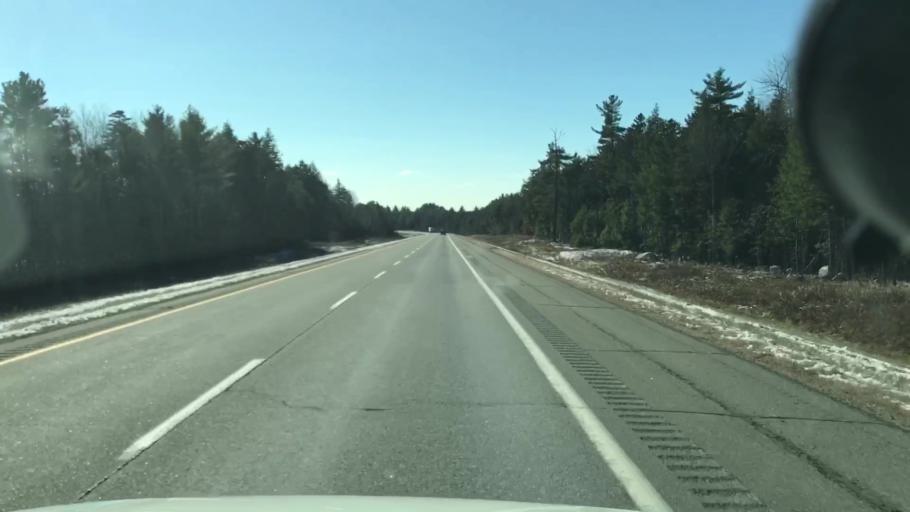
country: US
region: Maine
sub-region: Penobscot County
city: Howland
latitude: 45.2771
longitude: -68.6748
